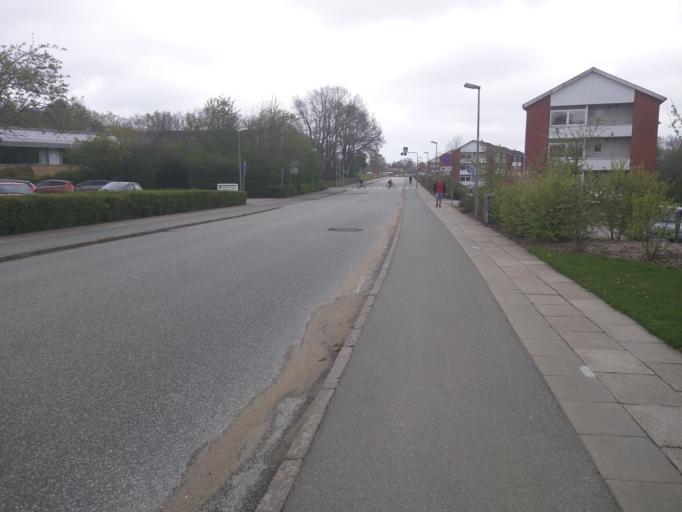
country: DK
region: Central Jutland
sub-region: Viborg Kommune
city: Viborg
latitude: 56.4625
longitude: 9.4093
